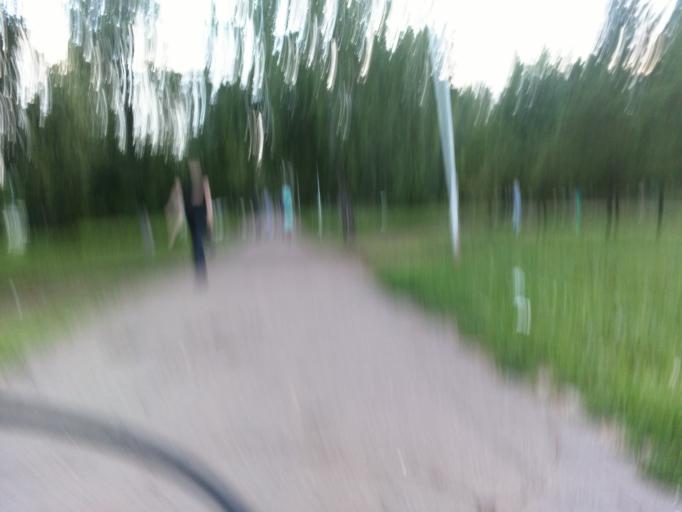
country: RU
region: Tatarstan
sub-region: Tukayevskiy Rayon
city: Naberezhnyye Chelny
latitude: 55.7484
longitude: 52.4160
